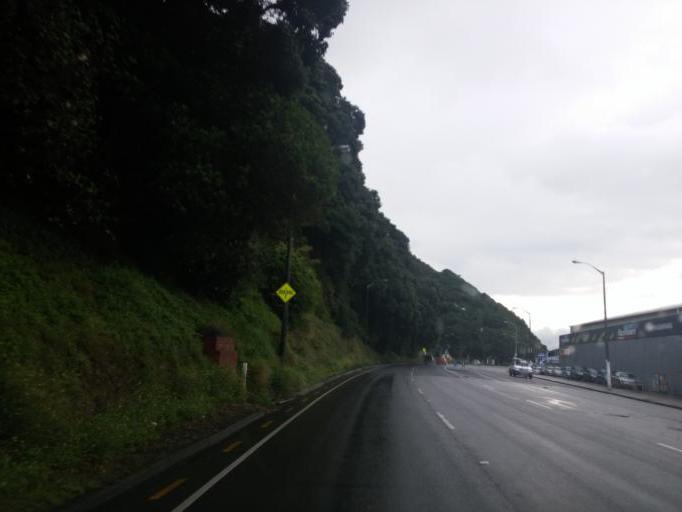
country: NZ
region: Wellington
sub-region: Wellington City
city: Wellington
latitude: -41.2567
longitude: 174.7943
